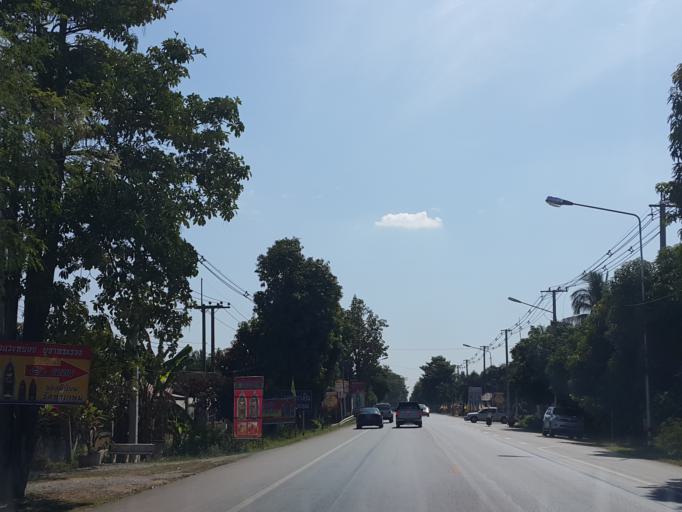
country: TH
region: Sukhothai
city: Si Samrong
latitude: 17.2261
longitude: 99.8596
